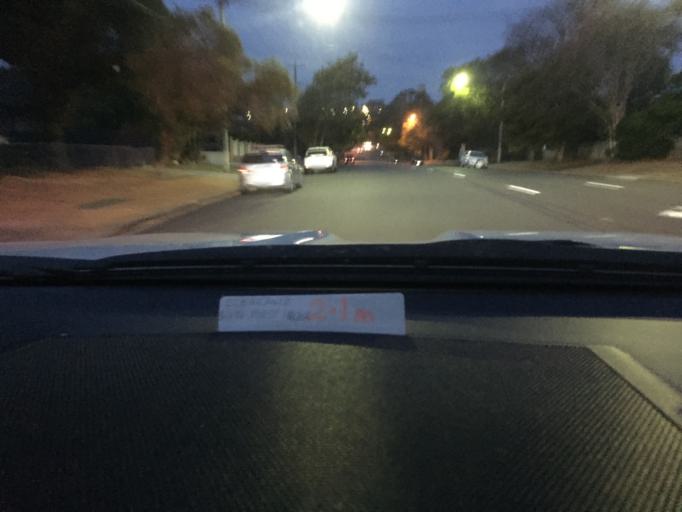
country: AU
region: Queensland
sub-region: Moreton Bay
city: Margate
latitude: -27.2428
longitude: 153.0920
